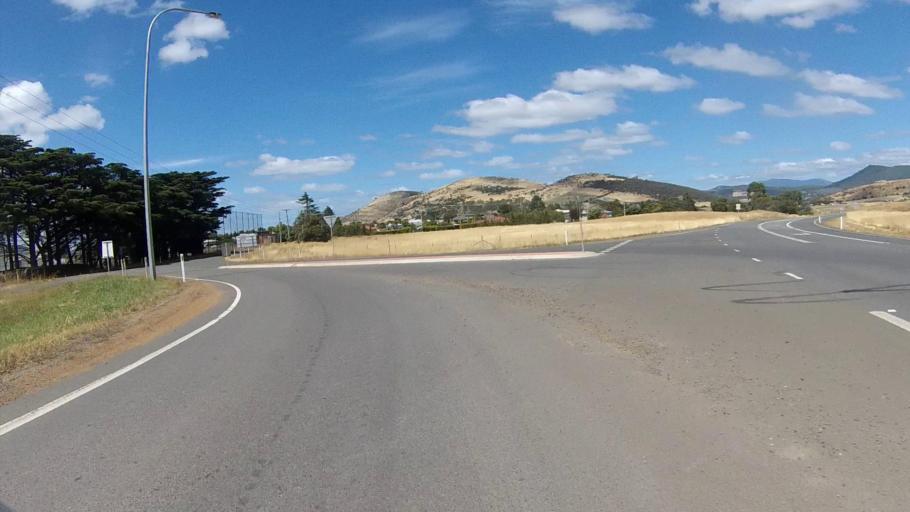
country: AU
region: Tasmania
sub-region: Clarence
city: Cambridge
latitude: -42.7288
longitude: 147.4357
